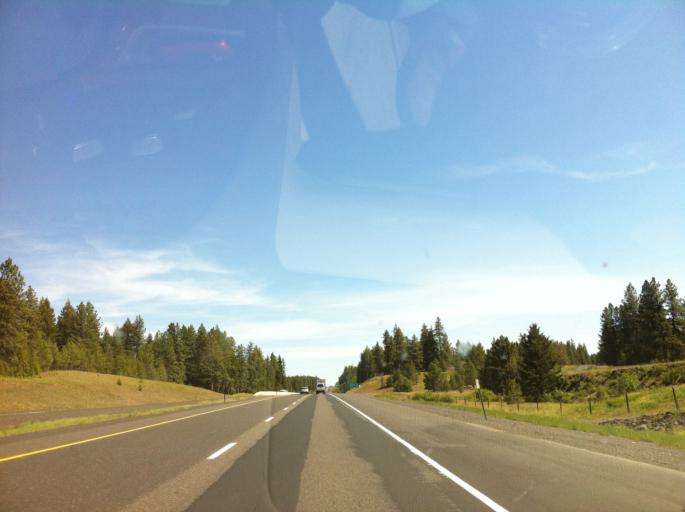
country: US
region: Oregon
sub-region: Umatilla County
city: Mission
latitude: 45.5007
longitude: -118.4210
